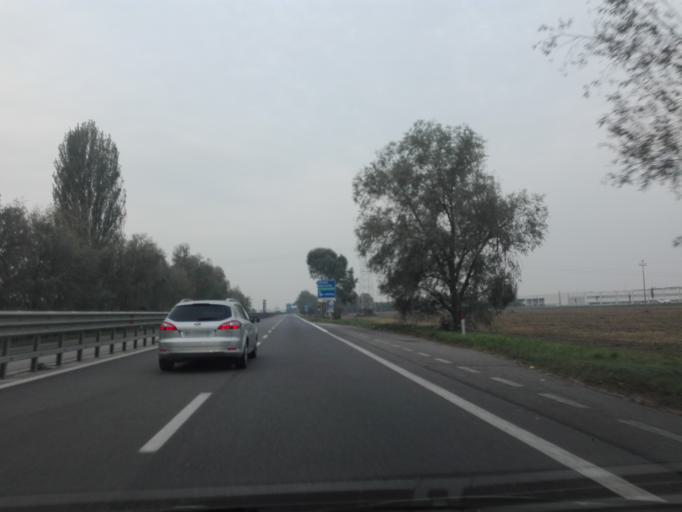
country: IT
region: Veneto
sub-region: Provincia di Rovigo
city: San Bellino
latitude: 45.0263
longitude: 11.5822
